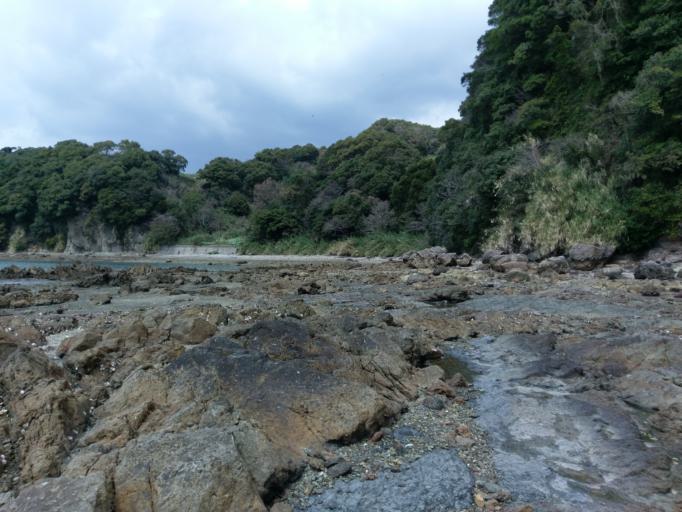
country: JP
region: Nagasaki
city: Nagasaki-shi
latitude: 32.7066
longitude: 129.9209
